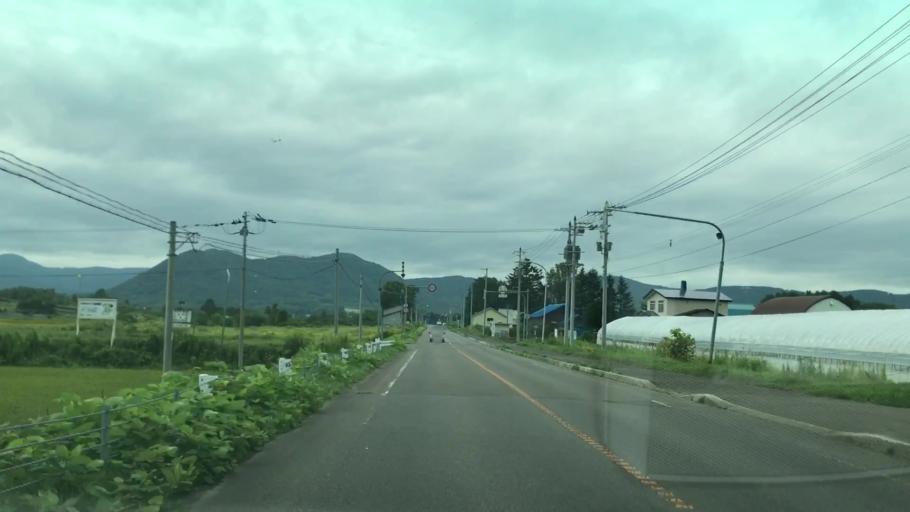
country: JP
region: Hokkaido
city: Yoichi
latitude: 43.0986
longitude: 140.8232
